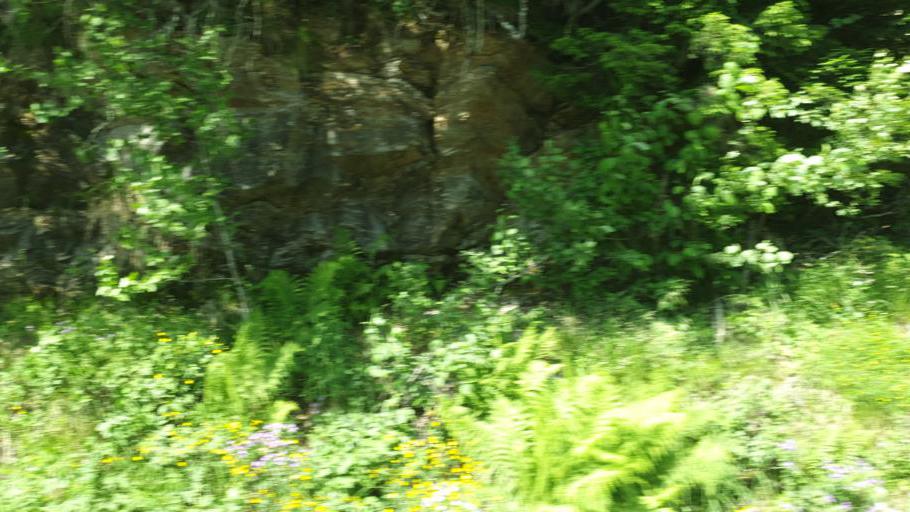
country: NO
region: Nord-Trondelag
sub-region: Leksvik
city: Leksvik
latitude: 63.6835
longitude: 10.6681
